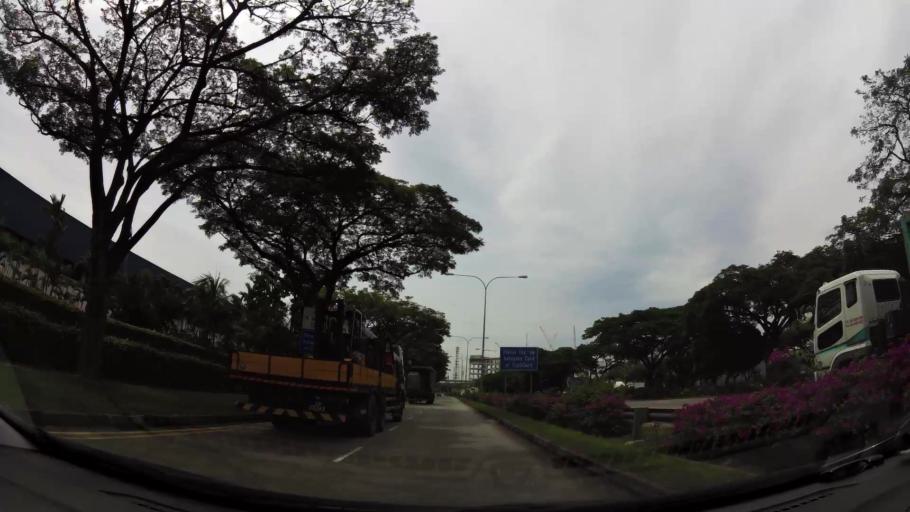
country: MY
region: Johor
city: Johor Bahru
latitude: 1.3219
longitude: 103.6692
